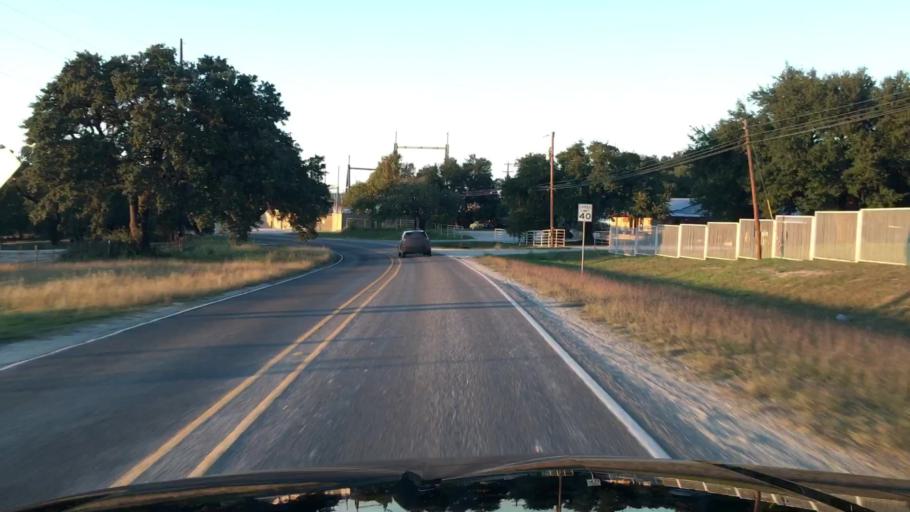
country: US
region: Texas
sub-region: Blanco County
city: Blanco
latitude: 30.0809
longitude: -98.4120
